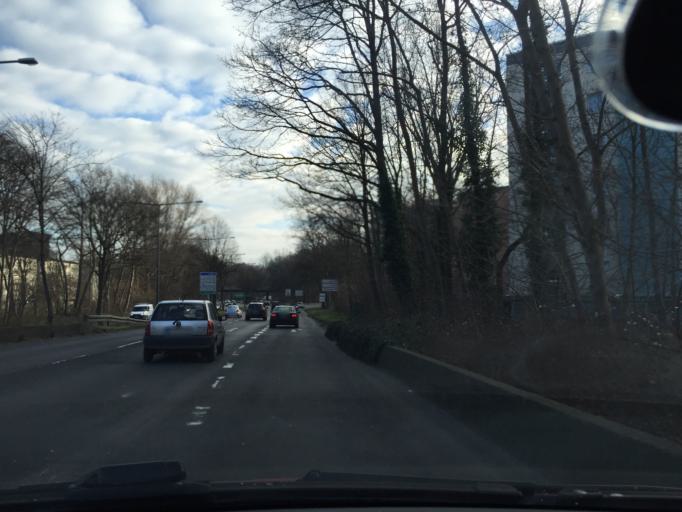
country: DE
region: North Rhine-Westphalia
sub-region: Regierungsbezirk Koln
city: Deutz
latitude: 50.9314
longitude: 6.9760
